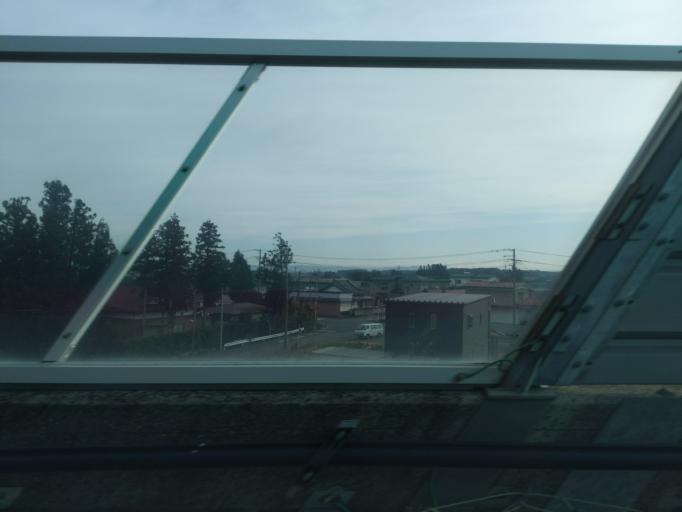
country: JP
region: Iwate
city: Ichinoseki
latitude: 38.7637
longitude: 141.0801
